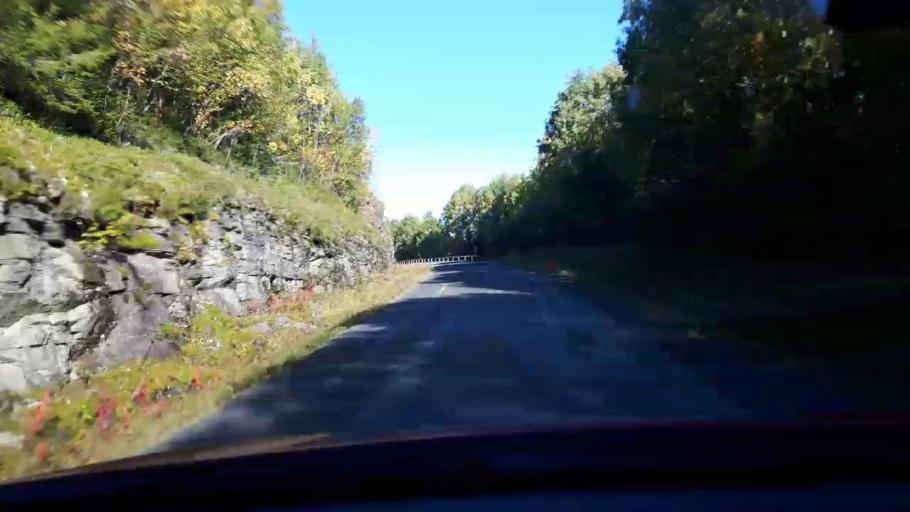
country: NO
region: Nord-Trondelag
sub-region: Lierne
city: Sandvika
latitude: 64.5720
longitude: 13.9024
